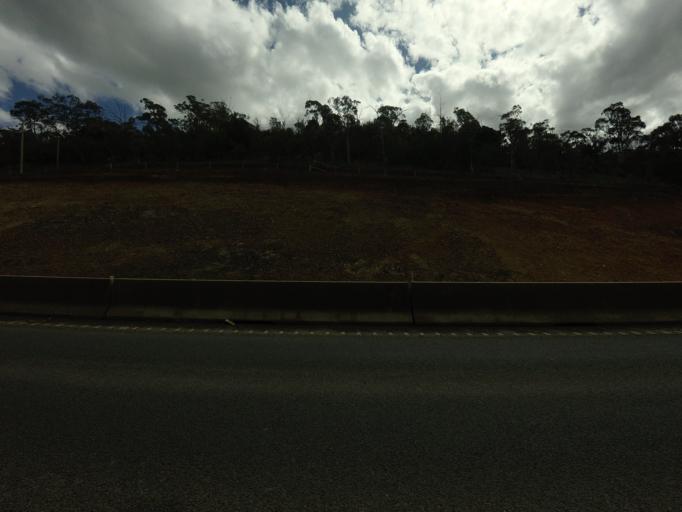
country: AU
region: Tasmania
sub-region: Brighton
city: Bridgewater
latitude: -42.2450
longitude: 147.4046
